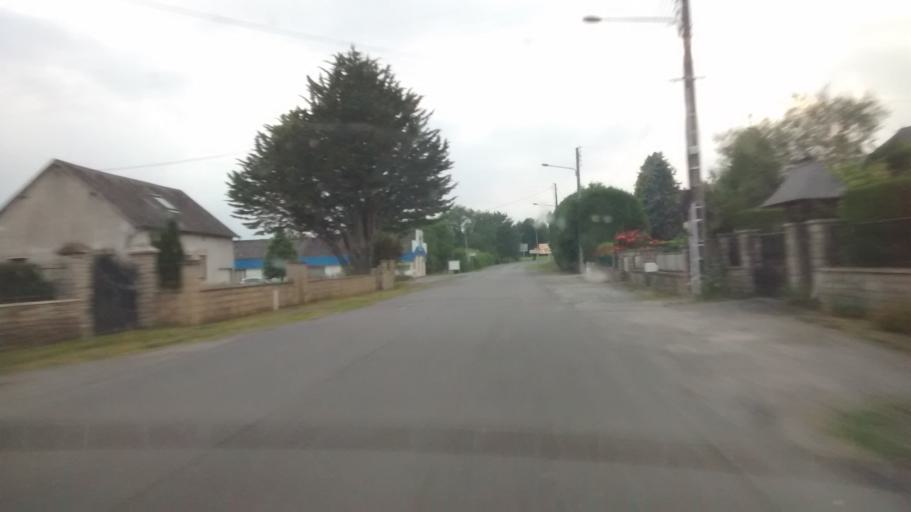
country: FR
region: Brittany
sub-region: Departement du Morbihan
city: Saint-Martin-sur-Oust
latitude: 47.7262
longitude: -2.2826
